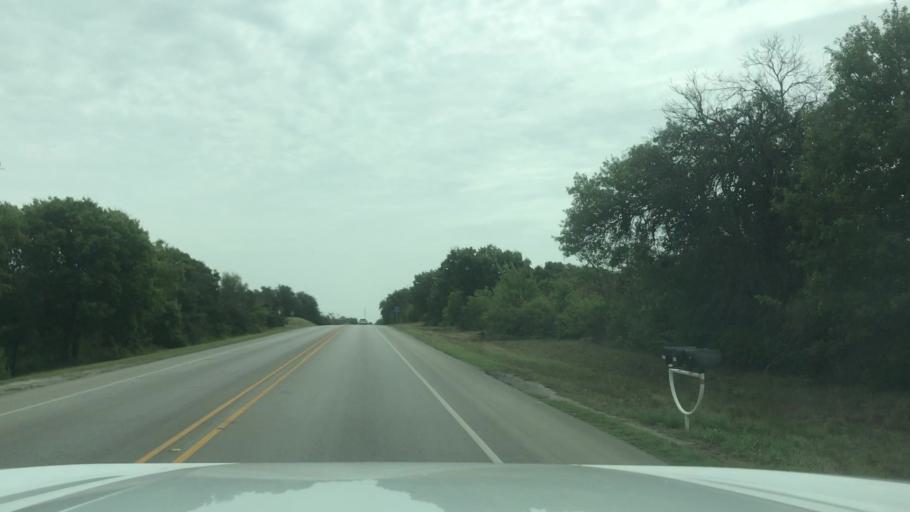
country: US
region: Texas
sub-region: Erath County
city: Dublin
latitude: 32.0982
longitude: -98.3914
